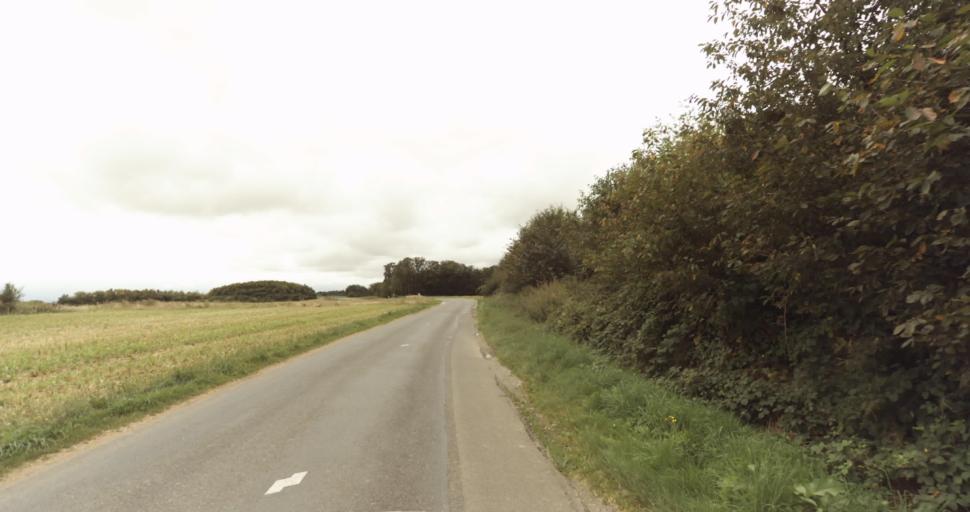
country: FR
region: Haute-Normandie
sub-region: Departement de l'Eure
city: Evreux
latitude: 48.9288
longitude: 1.2029
